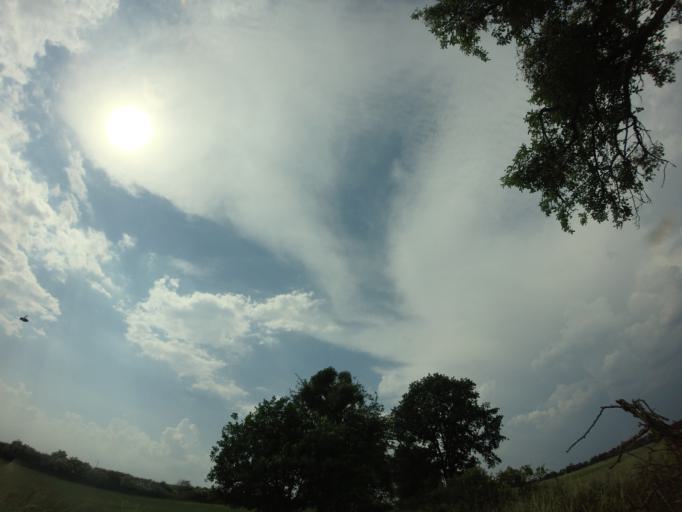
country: PL
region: West Pomeranian Voivodeship
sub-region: Powiat choszczenski
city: Krzecin
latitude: 53.1318
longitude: 15.5844
